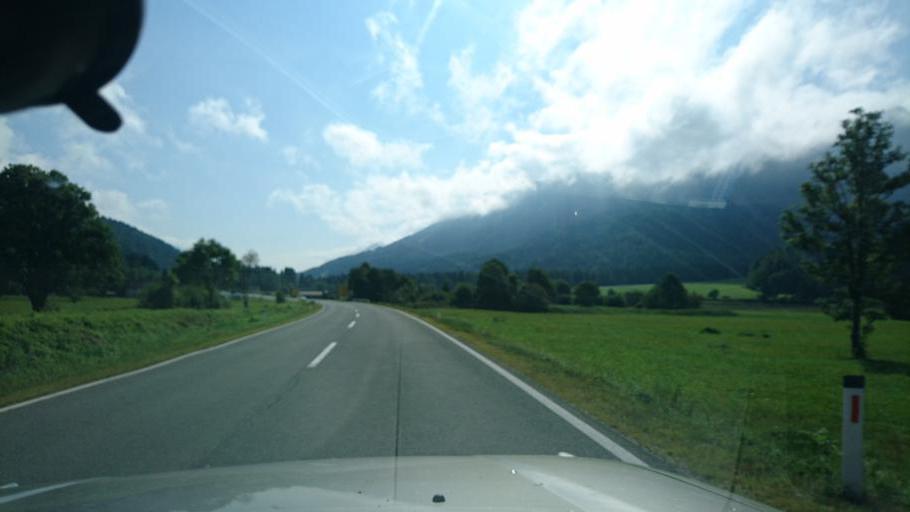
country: AT
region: Carinthia
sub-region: Politischer Bezirk Villach Land
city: Arnoldstein
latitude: 46.4948
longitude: 13.7151
